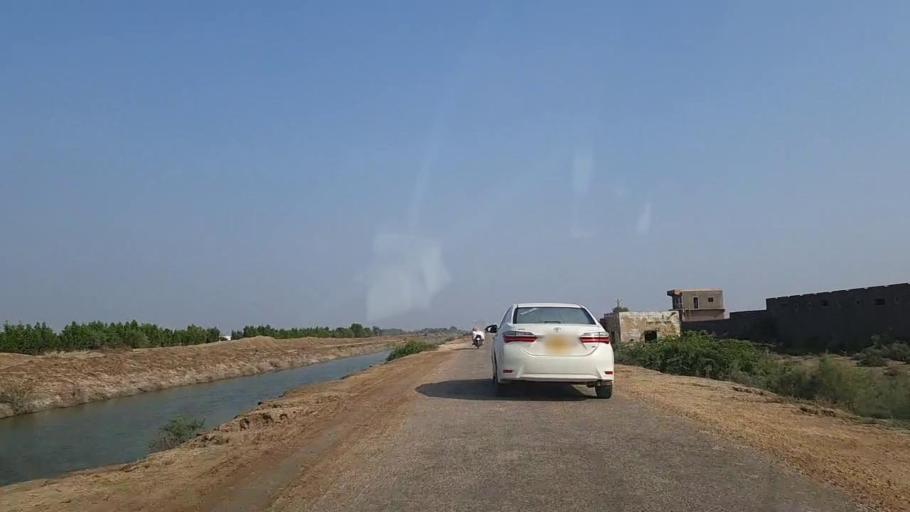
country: PK
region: Sindh
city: Mirpur Sakro
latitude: 24.6349
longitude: 67.6099
